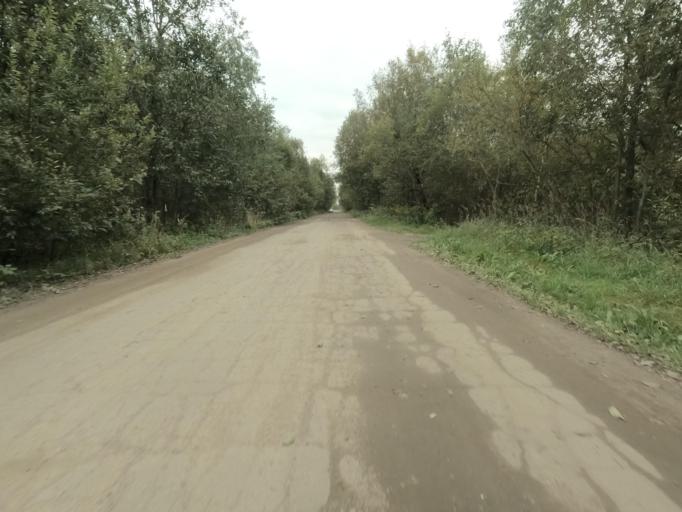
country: RU
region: St.-Petersburg
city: Sapernyy
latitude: 59.7612
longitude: 30.6523
